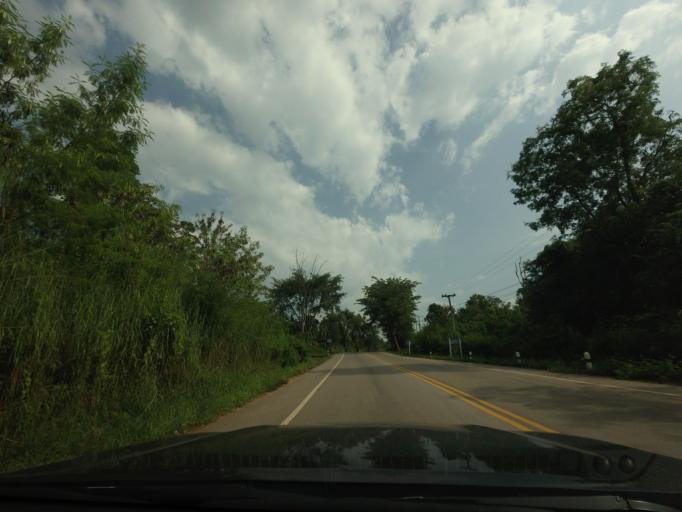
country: TH
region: Phitsanulok
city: Nakhon Thai
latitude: 17.0195
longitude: 100.9147
